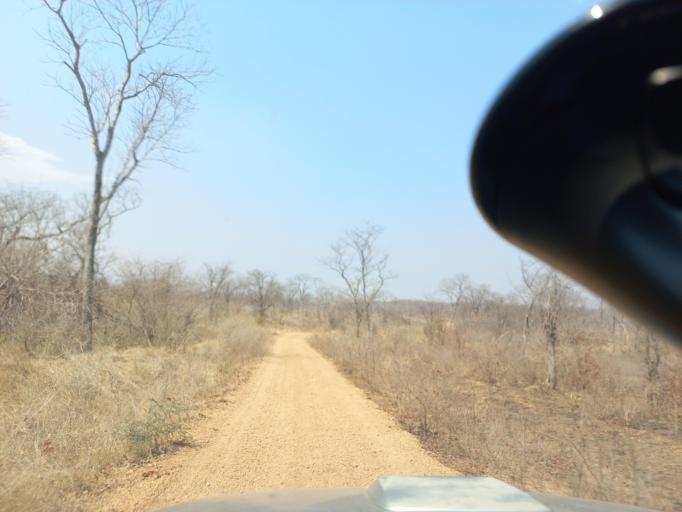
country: ZW
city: Chirundu
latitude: -15.9445
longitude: 28.7528
